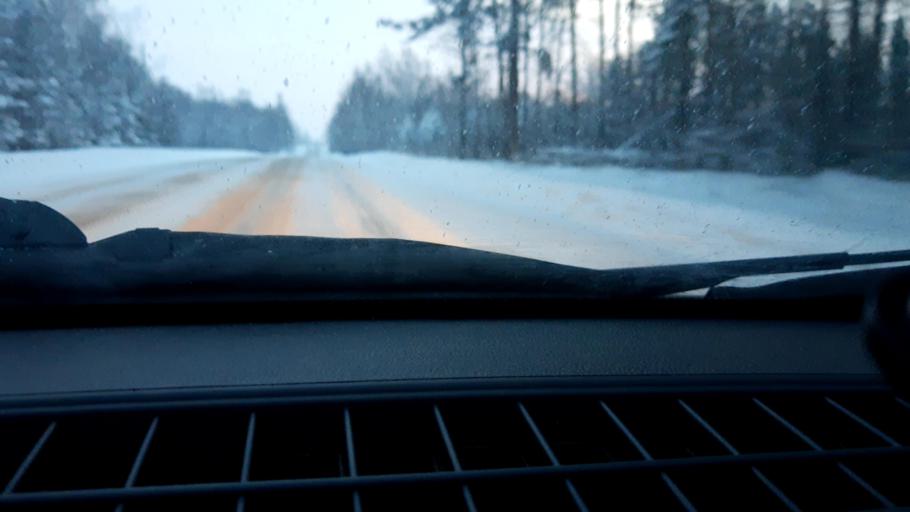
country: RU
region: Bashkortostan
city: Davlekanovo
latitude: 54.5665
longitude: 54.9679
